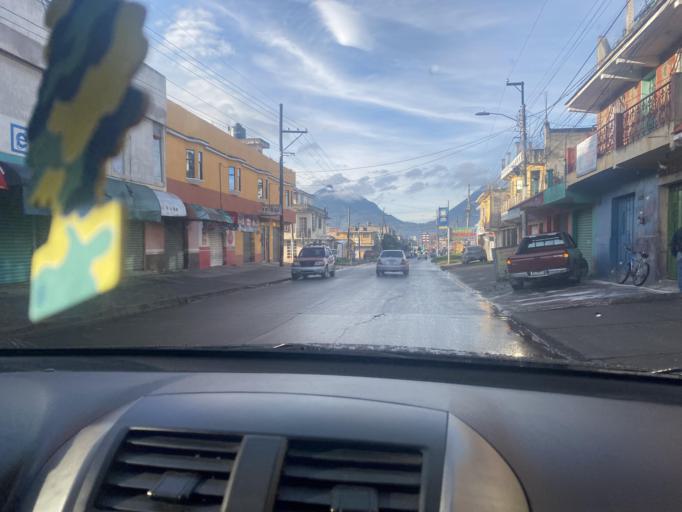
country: GT
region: Quetzaltenango
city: Olintepeque
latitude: 14.8650
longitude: -91.5214
